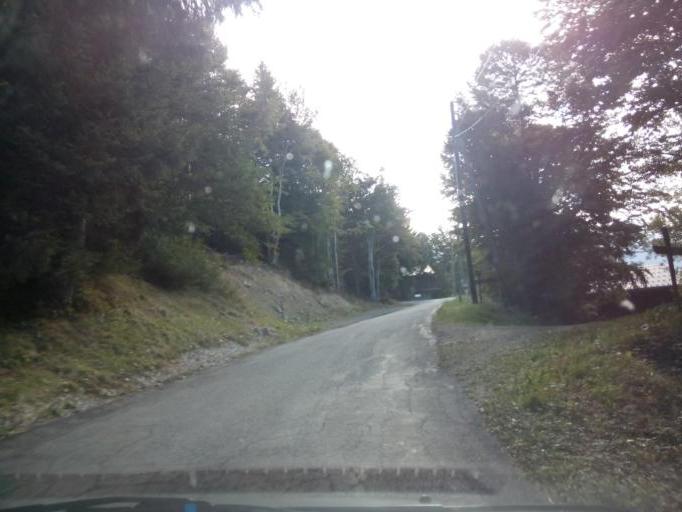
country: FR
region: Rhone-Alpes
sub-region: Departement de l'Isere
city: Vaulnaveys-le-Bas
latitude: 45.0360
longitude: 5.8566
